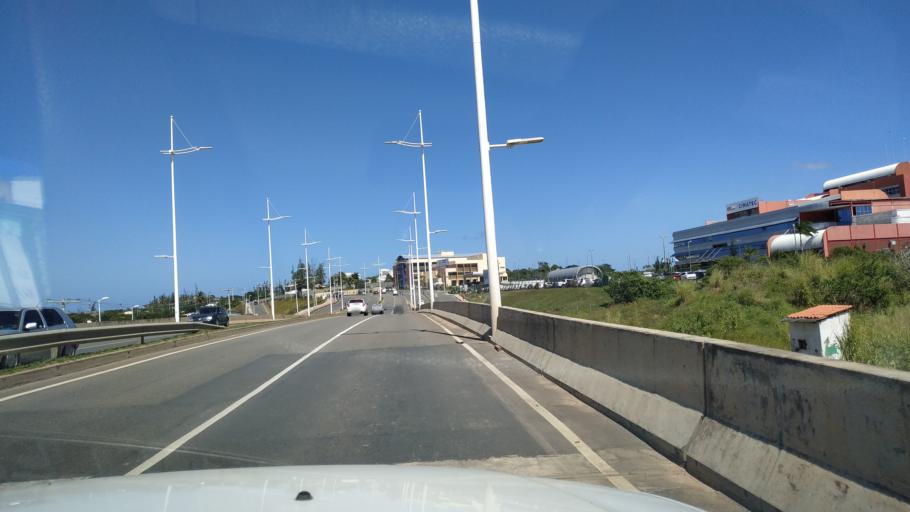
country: BR
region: Bahia
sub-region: Lauro De Freitas
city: Lauro de Freitas
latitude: -12.9372
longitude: -38.3857
